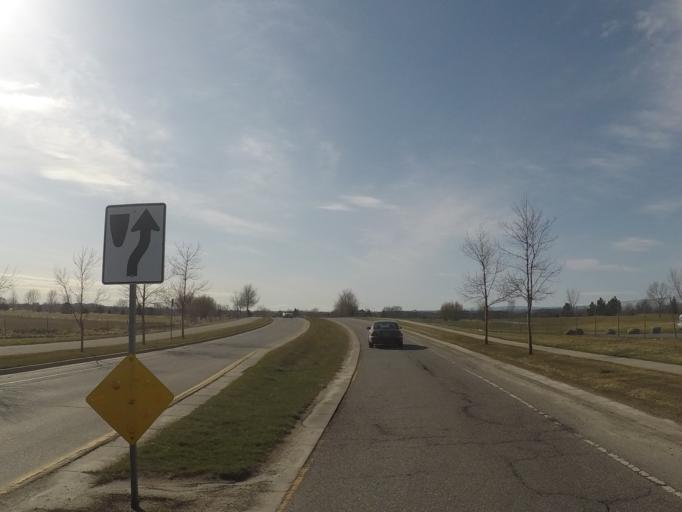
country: US
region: Montana
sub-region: Yellowstone County
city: Billings
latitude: 45.7812
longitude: -108.6001
